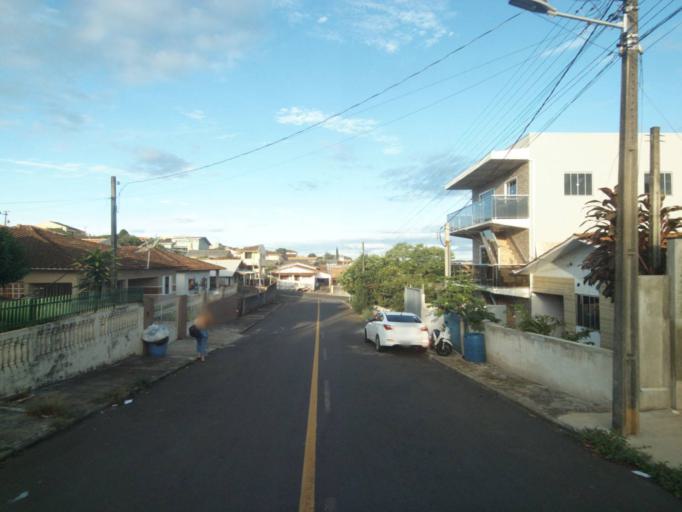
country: BR
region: Parana
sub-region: Telemaco Borba
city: Telemaco Borba
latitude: -24.3246
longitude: -50.6409
